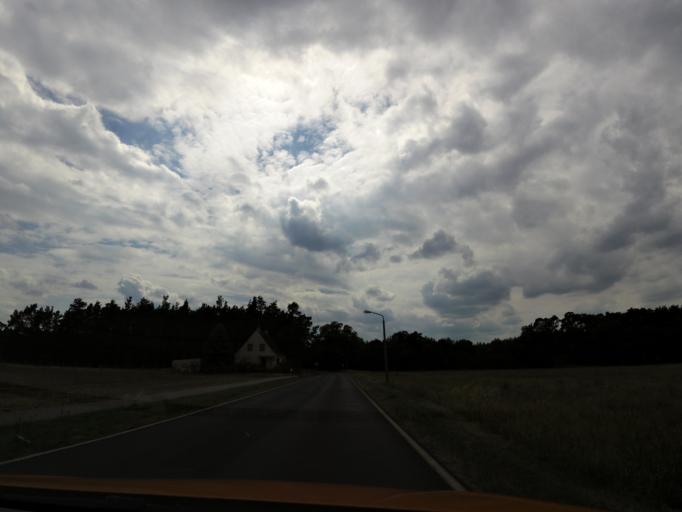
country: DE
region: Brandenburg
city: Baruth
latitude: 52.0246
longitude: 13.5492
